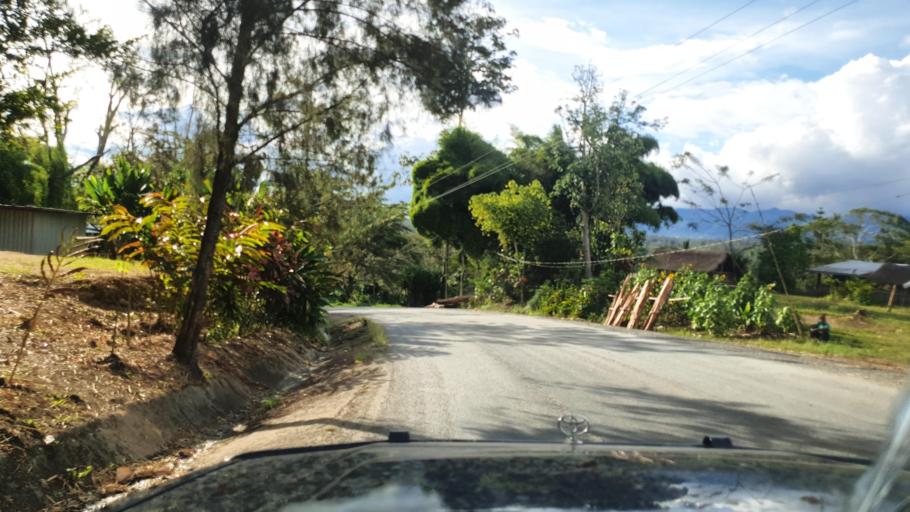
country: PG
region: Jiwaka
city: Minj
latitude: -5.8711
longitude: 144.6594
